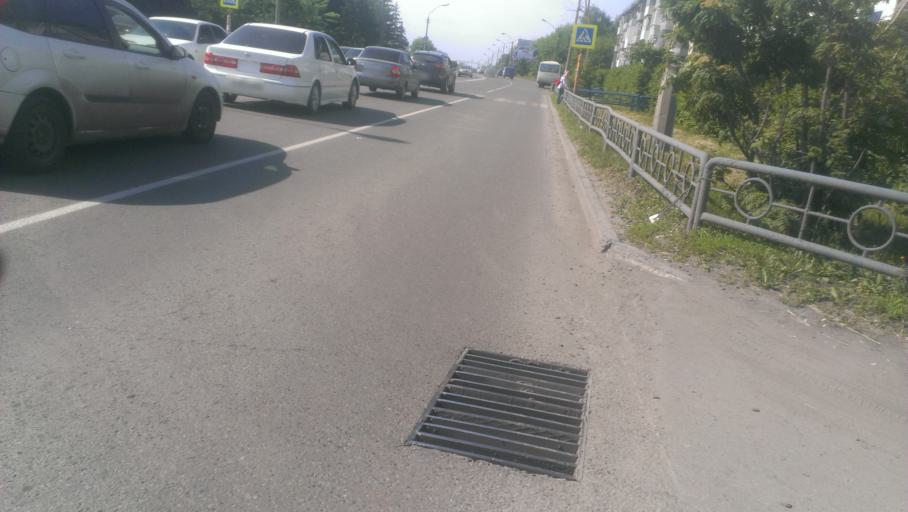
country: RU
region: Altai Krai
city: Novoaltaysk
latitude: 53.3931
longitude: 83.9338
